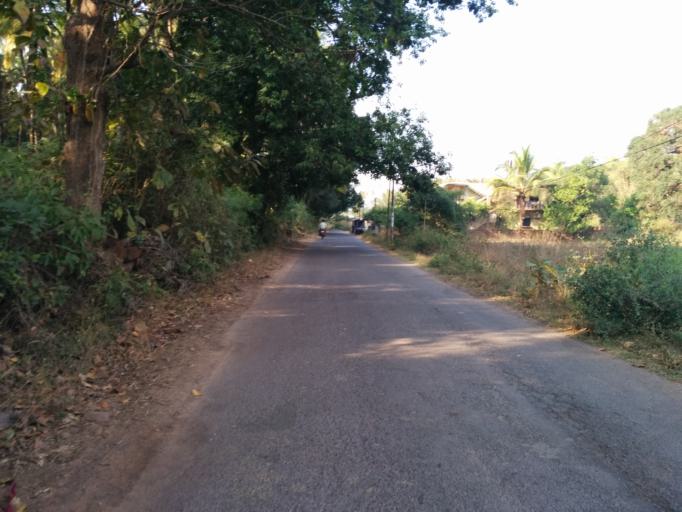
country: IN
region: Karnataka
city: Canacona
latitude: 15.0080
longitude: 74.0299
